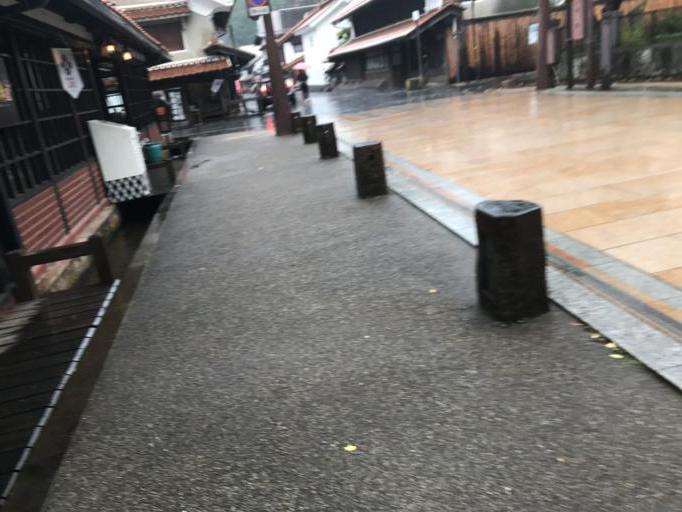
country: JP
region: Shimane
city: Masuda
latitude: 34.4677
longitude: 131.7738
